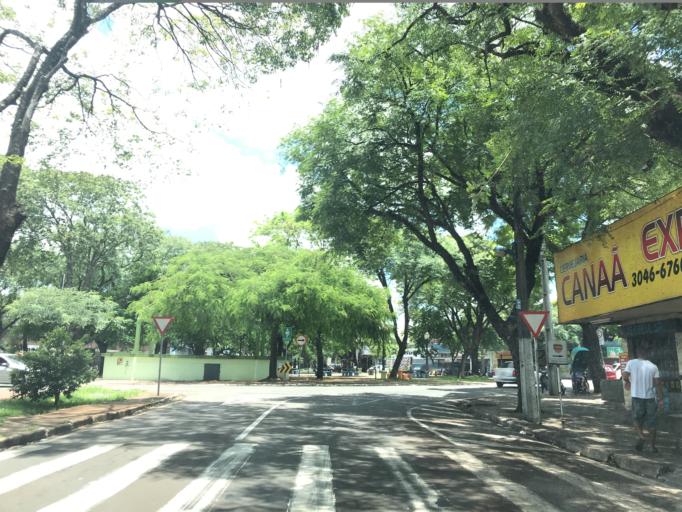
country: BR
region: Parana
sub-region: Maringa
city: Maringa
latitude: -23.4007
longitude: -51.9203
